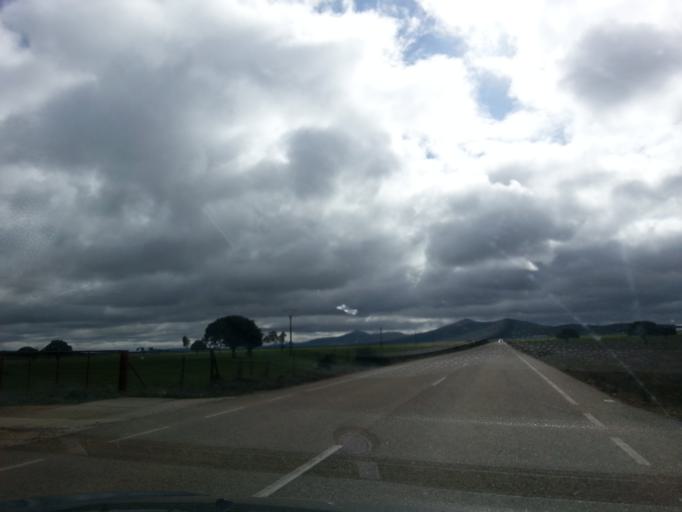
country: ES
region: Castille and Leon
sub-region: Provincia de Salamanca
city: Tamames
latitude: 40.6792
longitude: -6.1278
